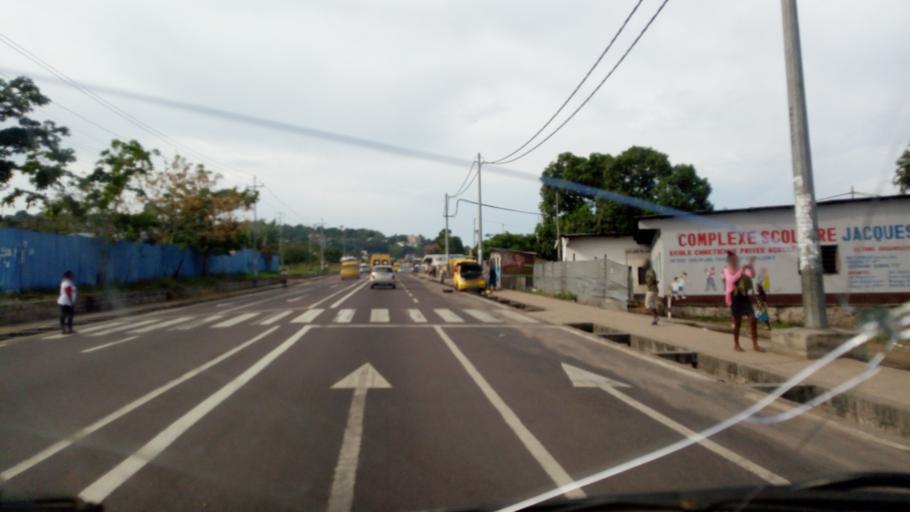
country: CD
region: Kinshasa
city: Kinshasa
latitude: -4.4286
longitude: 15.2579
